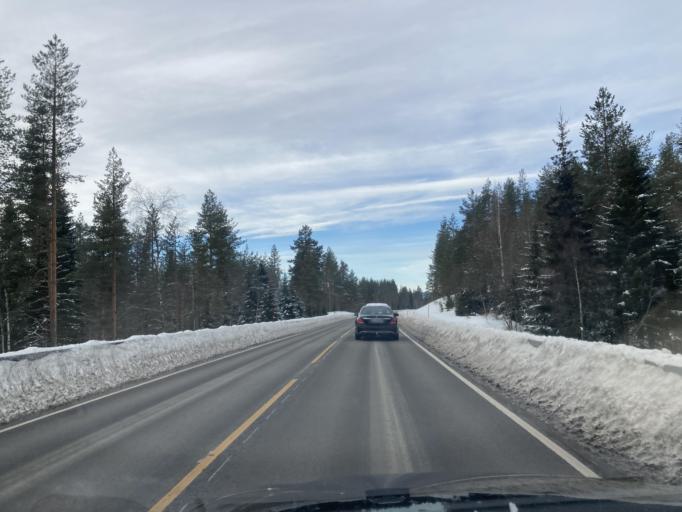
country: NO
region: Hedmark
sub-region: Trysil
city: Innbygda
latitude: 61.1779
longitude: 12.1821
